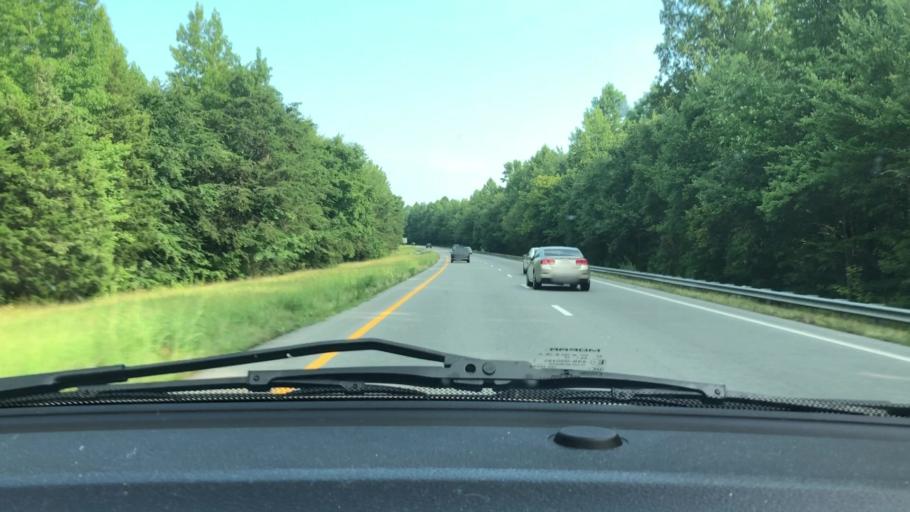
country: US
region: North Carolina
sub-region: Randolph County
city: Liberty
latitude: 35.8697
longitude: -79.6295
